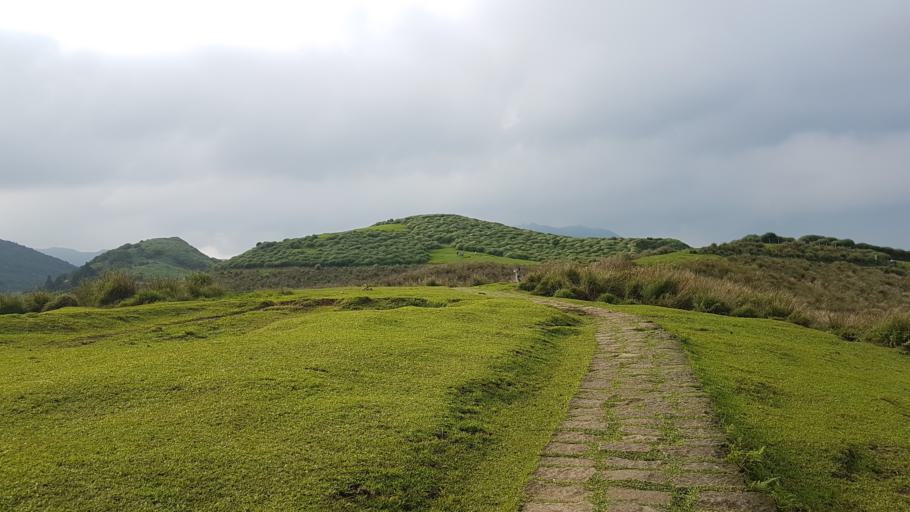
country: TW
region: Taipei
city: Taipei
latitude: 25.1645
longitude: 121.5781
